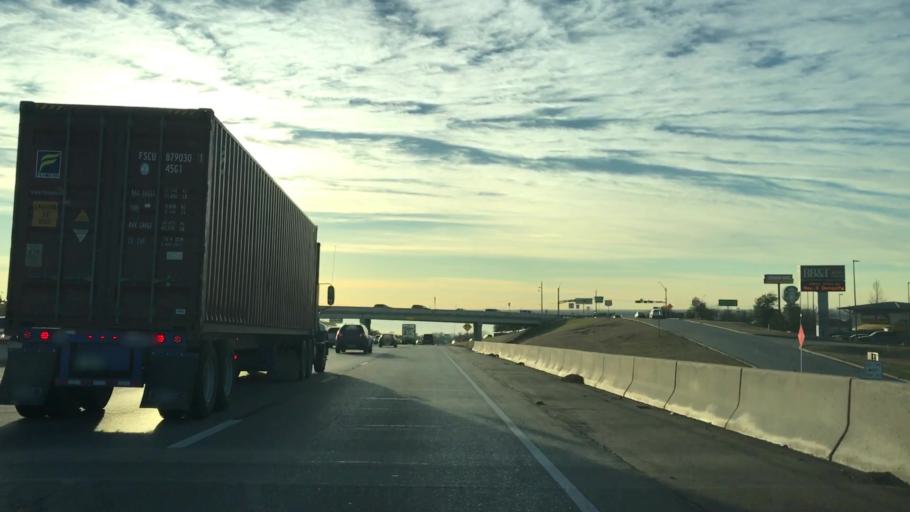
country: US
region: Texas
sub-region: Rockwall County
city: Rockwall
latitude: 32.8970
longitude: -96.4736
